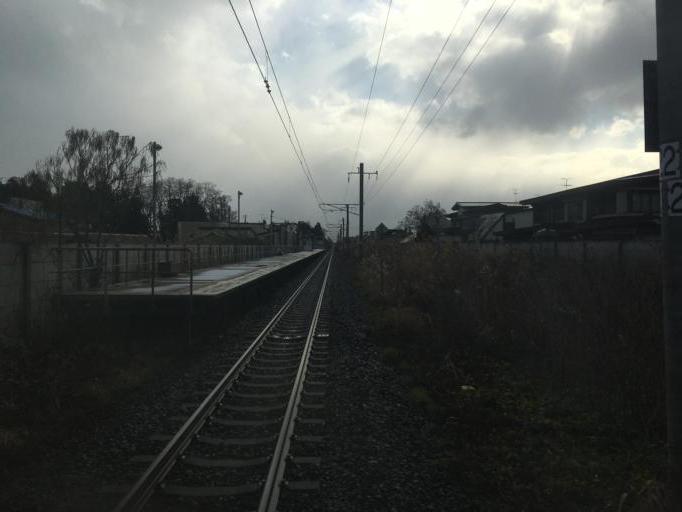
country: JP
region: Aomori
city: Aomori Shi
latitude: 40.8574
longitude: 140.6899
